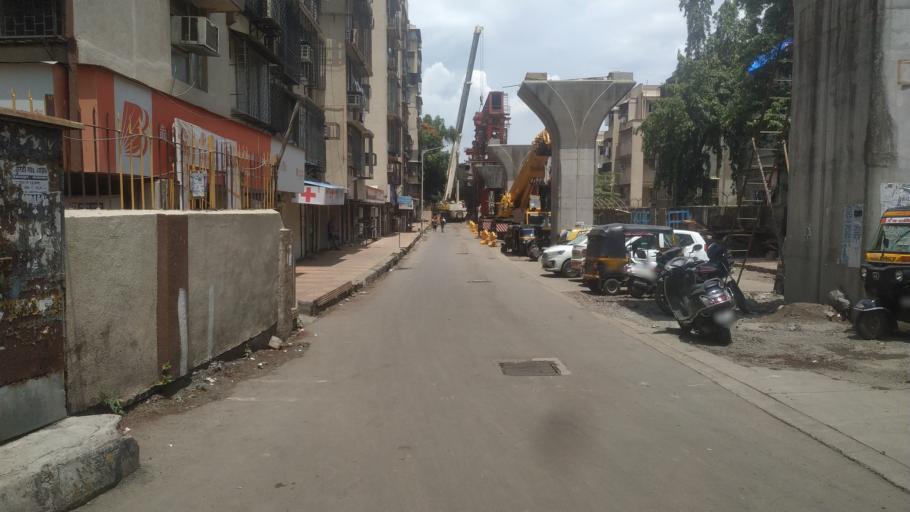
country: IN
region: Maharashtra
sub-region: Mumbai Suburban
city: Mumbai
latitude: 19.0522
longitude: 72.8677
